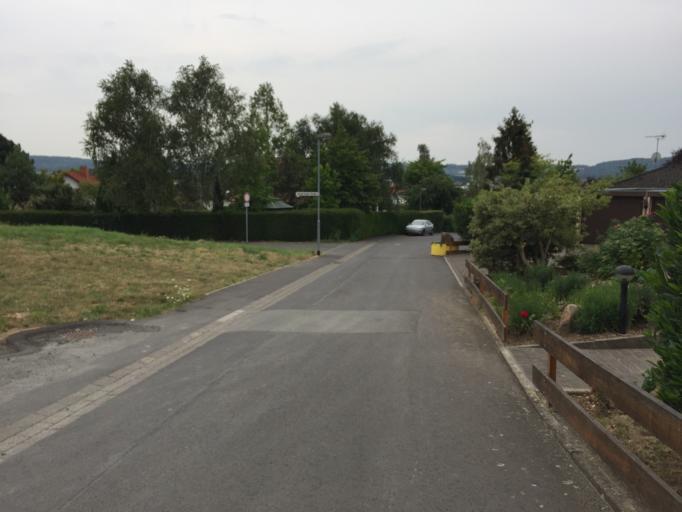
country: DE
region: Hesse
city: Staufenberg
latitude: 50.6638
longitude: 8.7354
